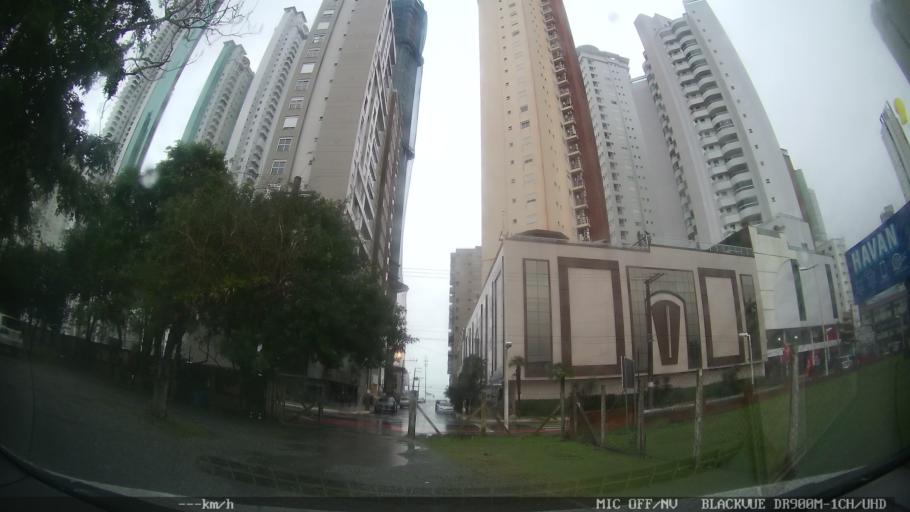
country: BR
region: Santa Catarina
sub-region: Balneario Camboriu
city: Balneario Camboriu
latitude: -27.0075
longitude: -48.6109
